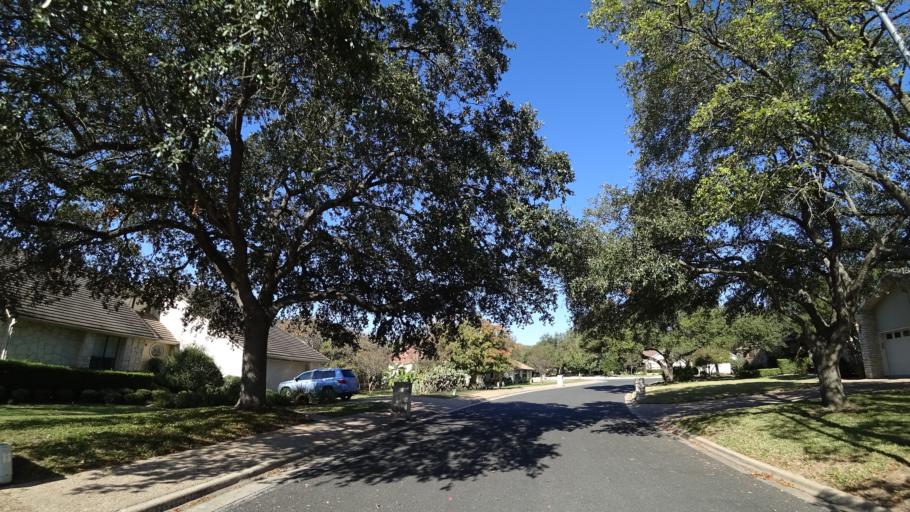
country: US
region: Texas
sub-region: Williamson County
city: Jollyville
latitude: 30.4055
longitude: -97.7608
